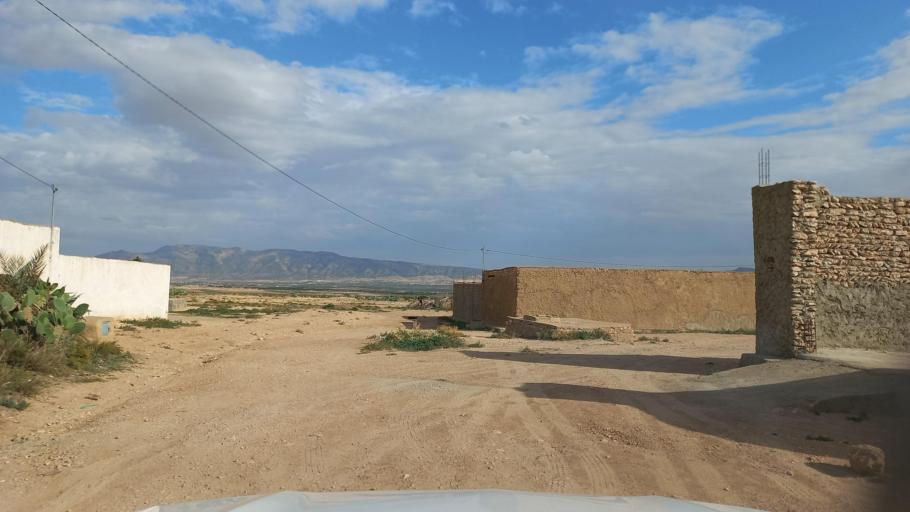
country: TN
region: Al Qasrayn
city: Sbiba
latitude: 35.4491
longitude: 9.0858
